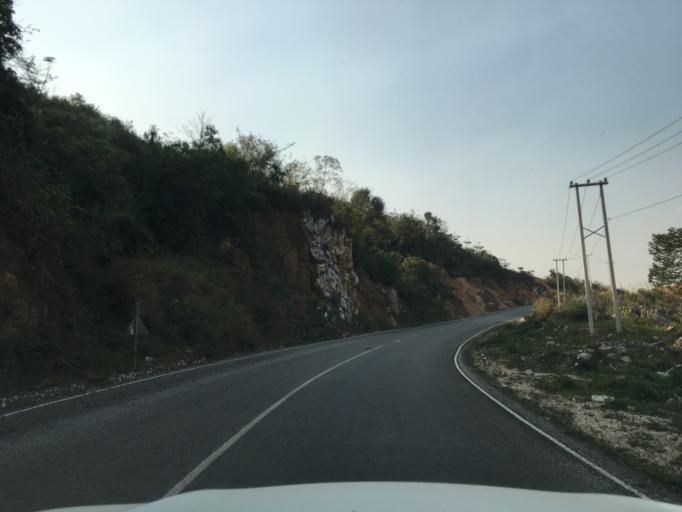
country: LA
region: Houaphan
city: Xam Nua
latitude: 20.5727
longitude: 104.0570
